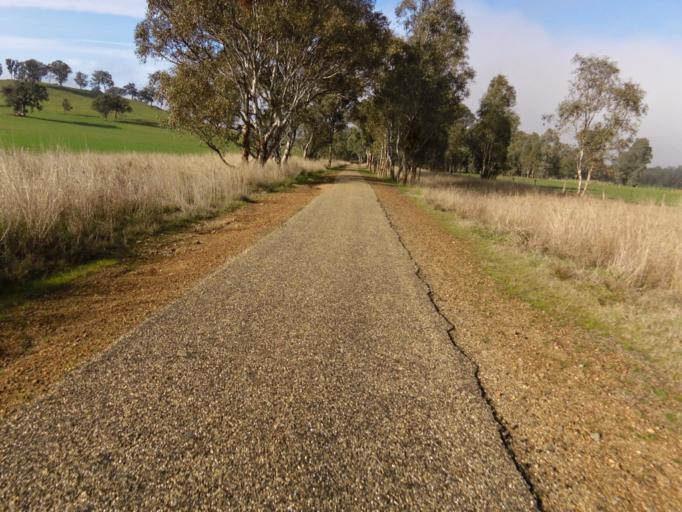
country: AU
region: Victoria
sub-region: Wangaratta
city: Wangaratta
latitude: -36.4441
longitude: 146.5512
